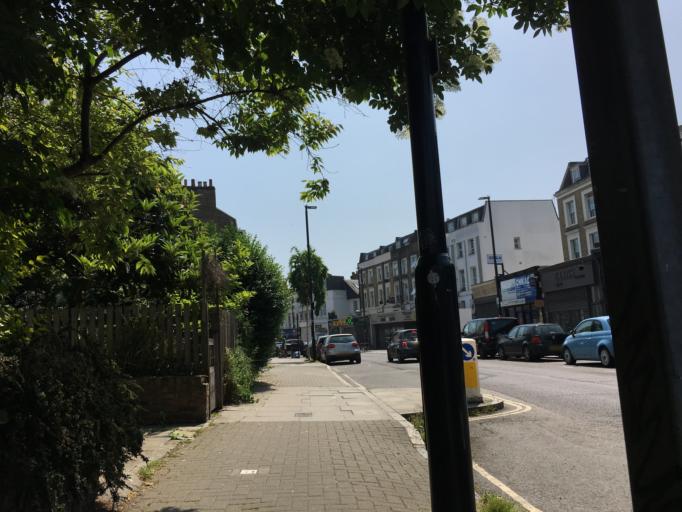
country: GB
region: England
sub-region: Greater London
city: Holloway
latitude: 51.5500
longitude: -0.1303
